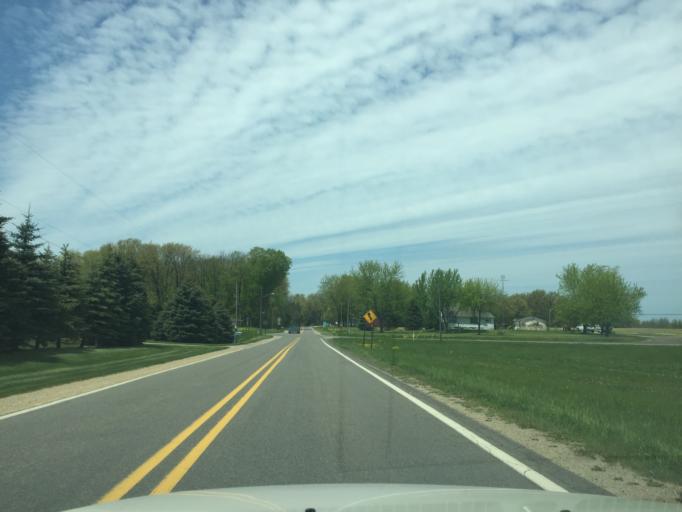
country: US
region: Michigan
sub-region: Berrien County
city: Stevensville
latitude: 41.9845
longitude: -86.4984
